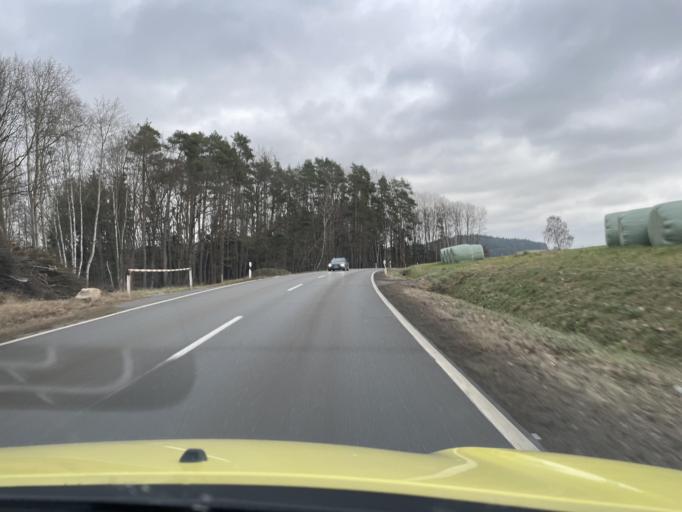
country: DE
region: Bavaria
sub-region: Upper Palatinate
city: Zandt
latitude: 49.1674
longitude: 12.7081
